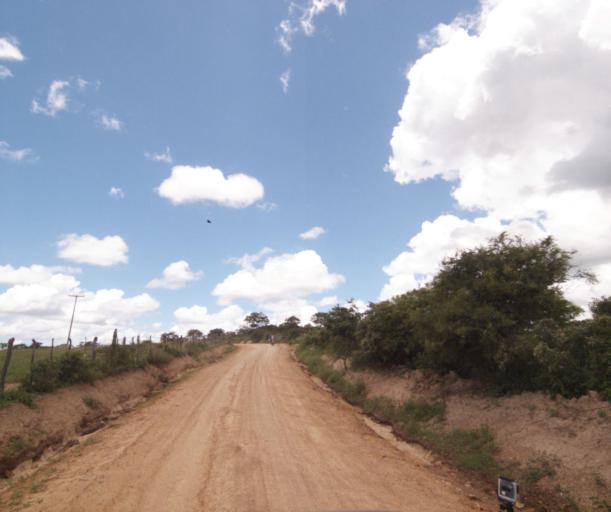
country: BR
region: Bahia
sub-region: Pocoes
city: Pocoes
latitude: -14.3788
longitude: -40.3621
